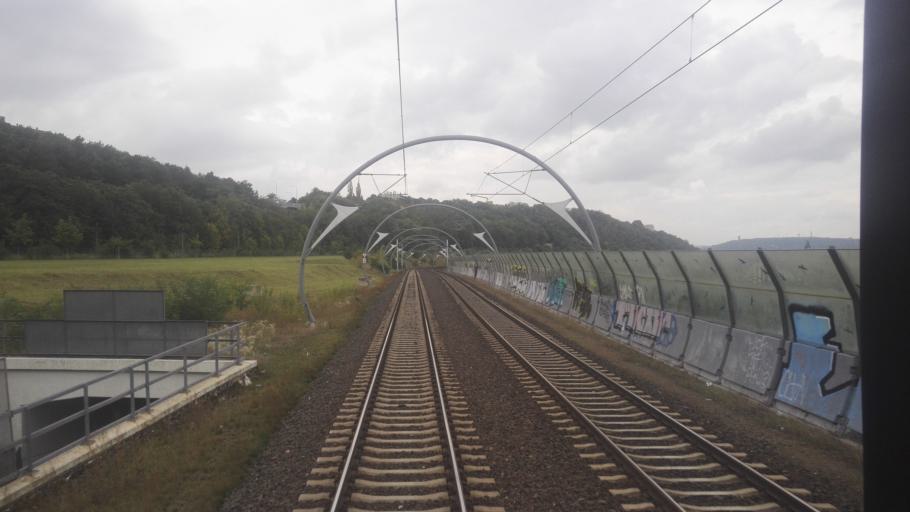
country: CZ
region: Praha
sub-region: Praha 8
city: Liben
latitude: 50.0947
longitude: 14.4721
